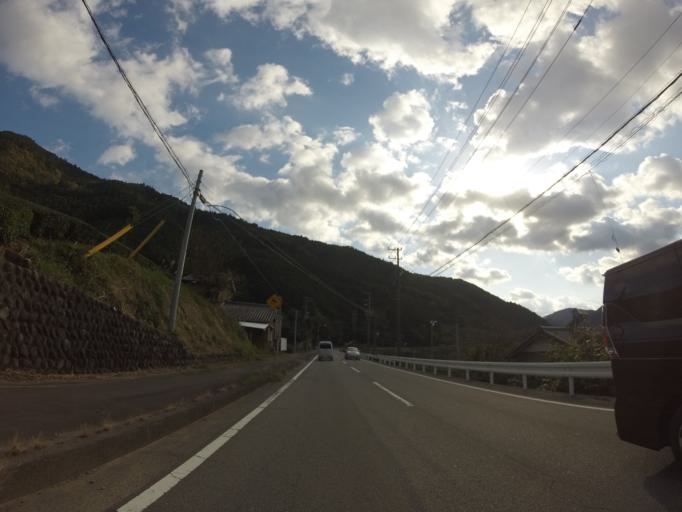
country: JP
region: Shizuoka
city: Kanaya
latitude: 34.8893
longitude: 138.1192
